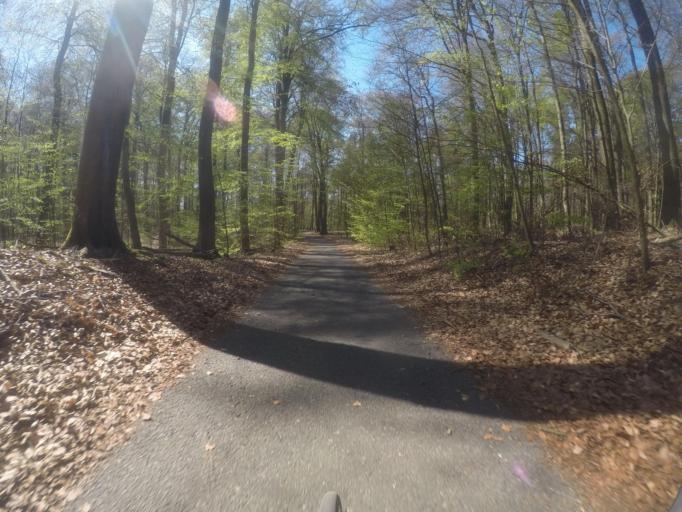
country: DE
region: Brandenburg
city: Wandlitz
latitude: 52.7523
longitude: 13.4963
